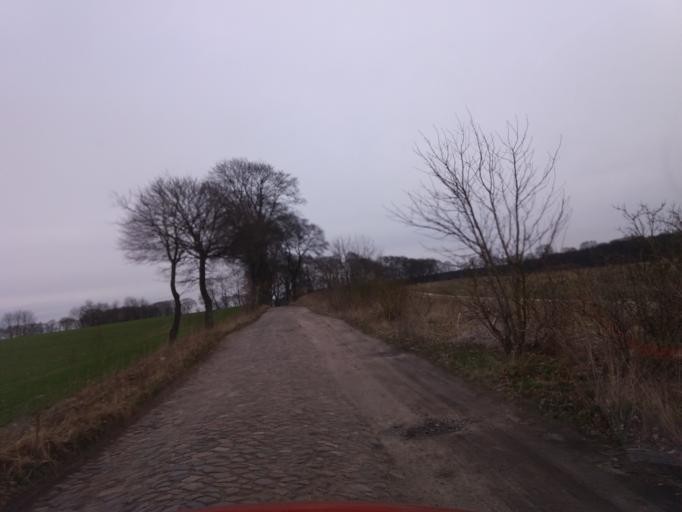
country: PL
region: West Pomeranian Voivodeship
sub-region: Powiat choszczenski
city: Recz
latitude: 53.1606
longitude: 15.6105
